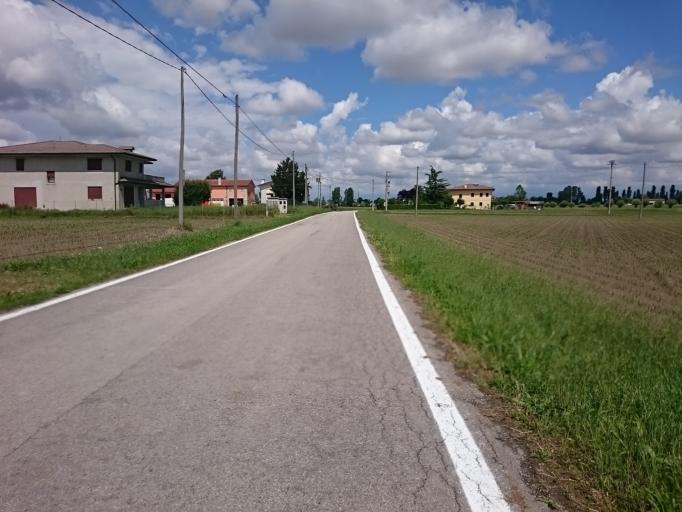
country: IT
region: Veneto
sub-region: Provincia di Padova
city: Campodoro
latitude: 45.4784
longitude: 11.7385
